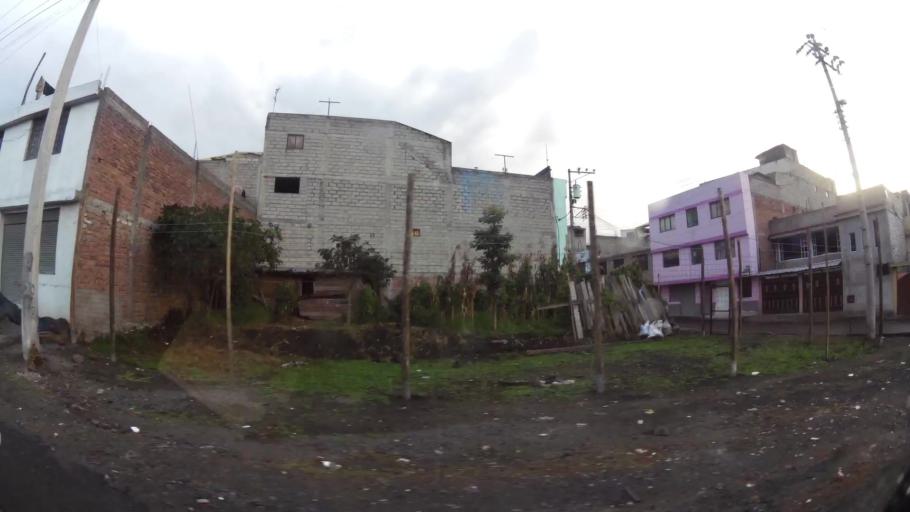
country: EC
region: Pichincha
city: Quito
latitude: -0.2994
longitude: -78.5391
